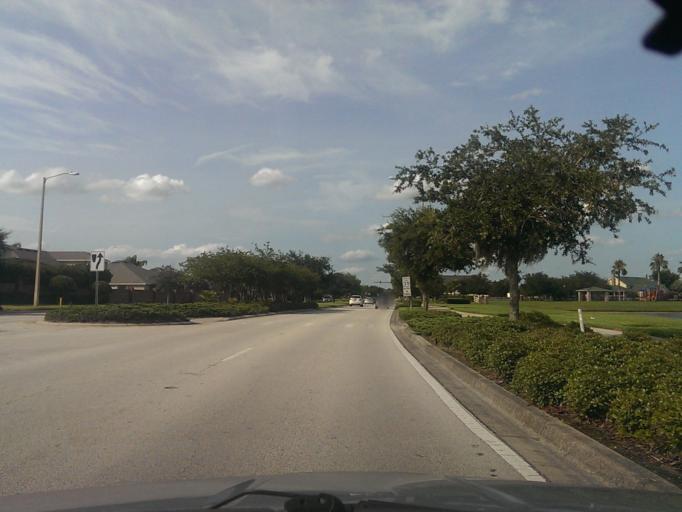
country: US
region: Florida
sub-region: Orange County
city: Winter Garden
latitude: 28.5280
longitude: -81.5845
